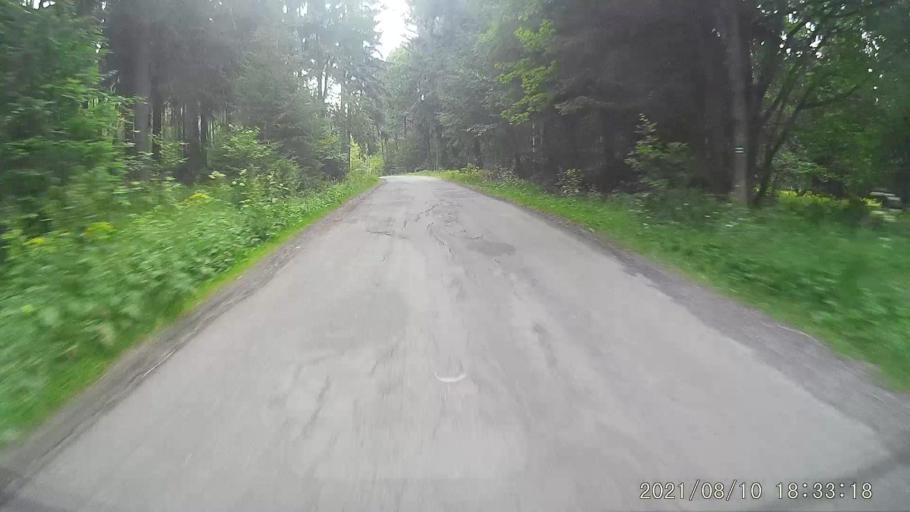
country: PL
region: Lower Silesian Voivodeship
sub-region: Powiat klodzki
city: Radkow
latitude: 50.4872
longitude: 16.3475
